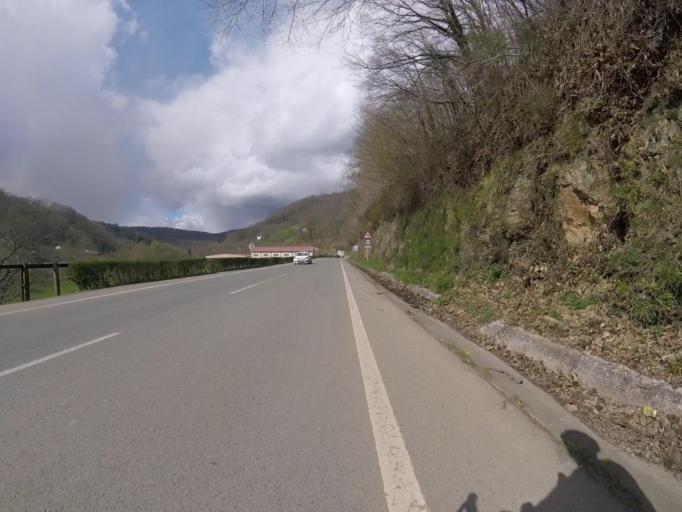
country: ES
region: Navarre
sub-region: Provincia de Navarra
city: Etxalar
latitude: 43.2357
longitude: -1.6400
